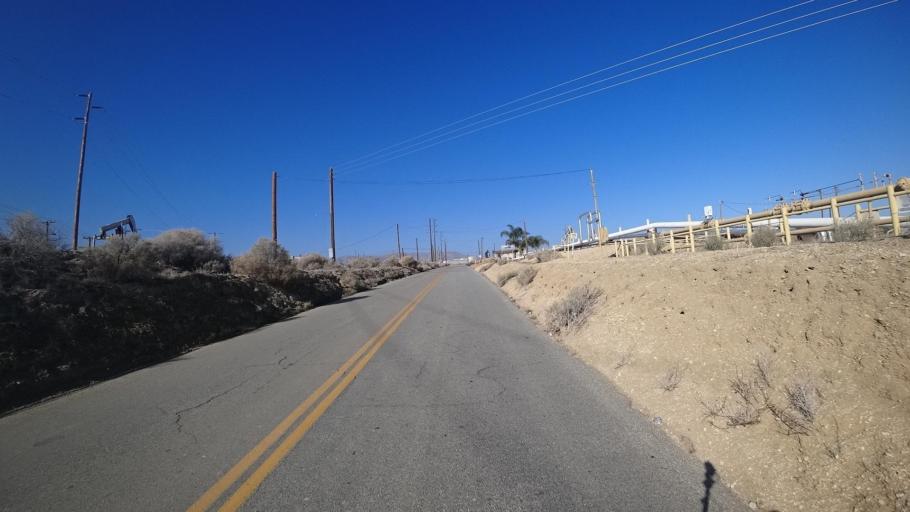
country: US
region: California
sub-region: Kern County
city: Taft Heights
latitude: 35.2246
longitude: -119.6236
